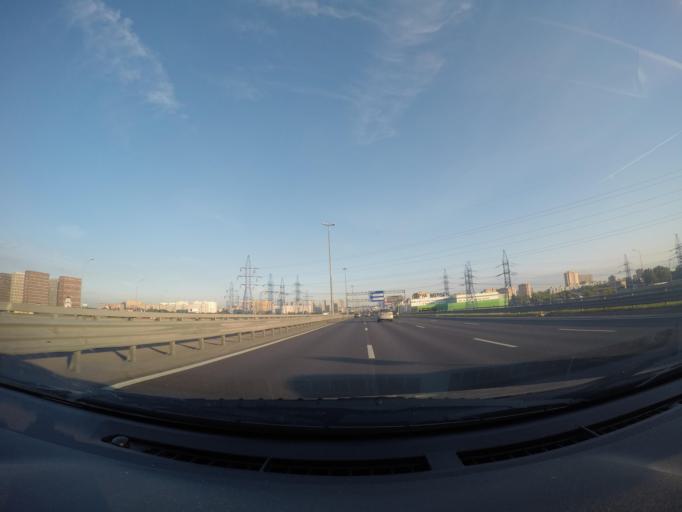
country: RU
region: Moskovskaya
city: Lyubertsy
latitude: 55.6618
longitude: 37.8872
